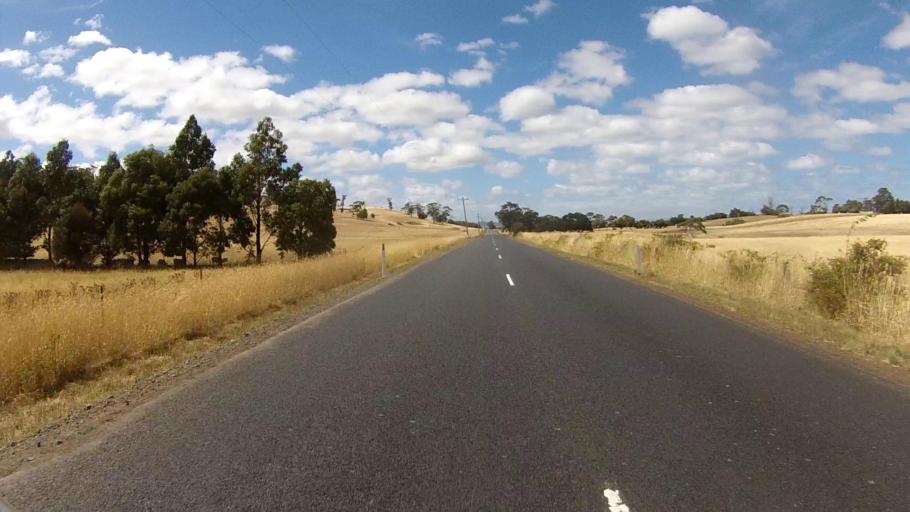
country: AU
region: Tasmania
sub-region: Sorell
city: Sorell
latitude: -42.7532
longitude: 147.5045
